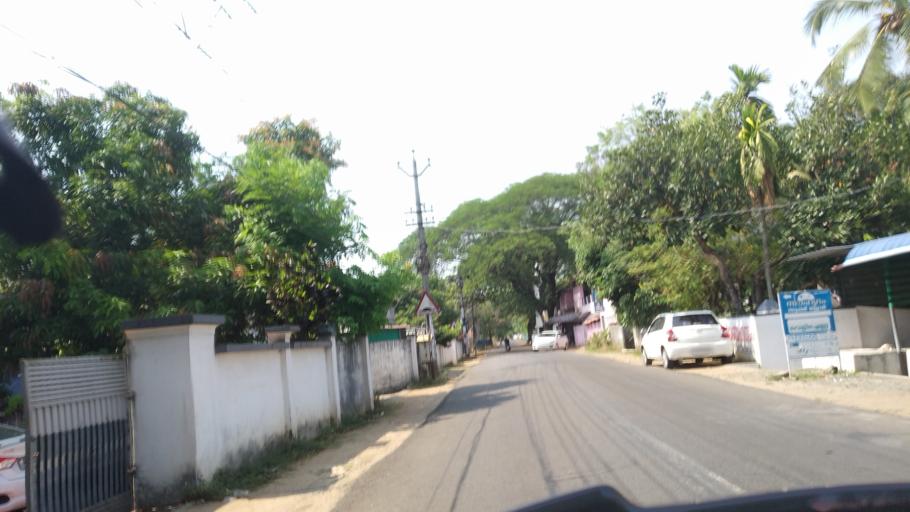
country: IN
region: Kerala
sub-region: Thrissur District
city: Thanniyam
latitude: 10.3404
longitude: 76.1173
